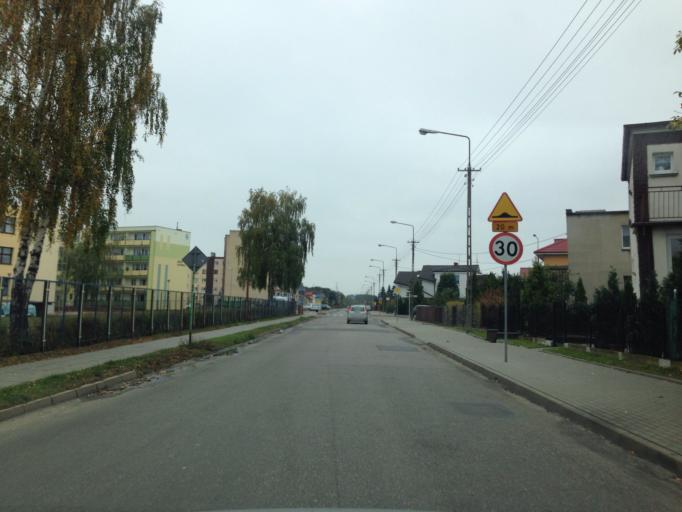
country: PL
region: Kujawsko-Pomorskie
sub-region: Grudziadz
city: Grudziadz
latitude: 53.4278
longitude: 18.7274
